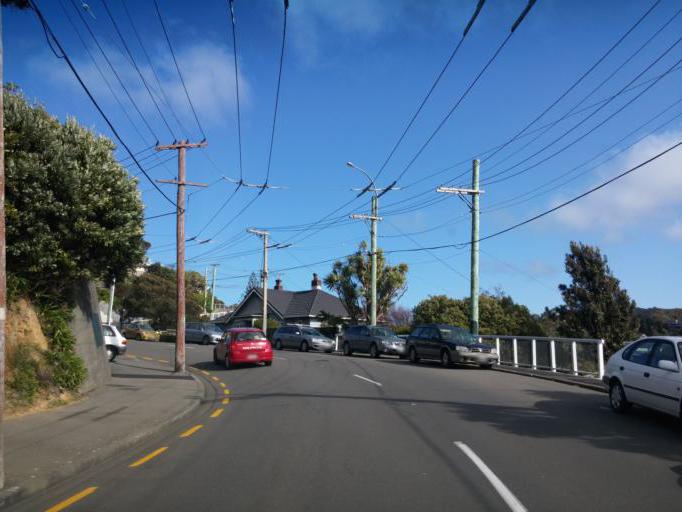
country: NZ
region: Wellington
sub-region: Wellington City
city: Brooklyn
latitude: -41.3084
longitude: 174.7662
